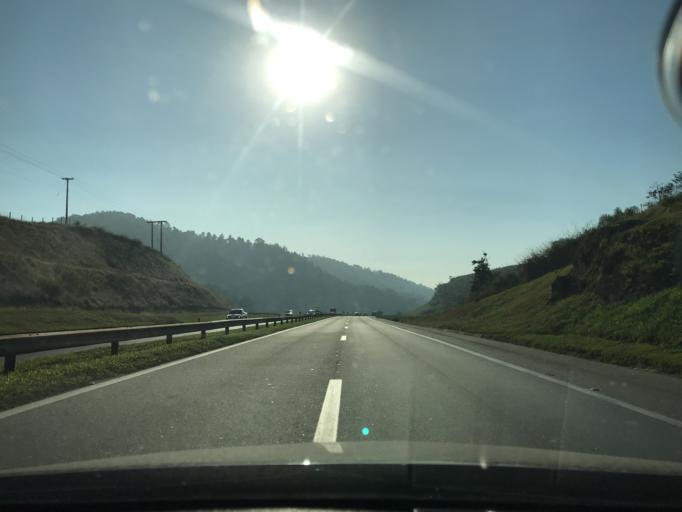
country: BR
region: Sao Paulo
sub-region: Santa Isabel
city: Santa Isabel
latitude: -23.3614
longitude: -46.2199
